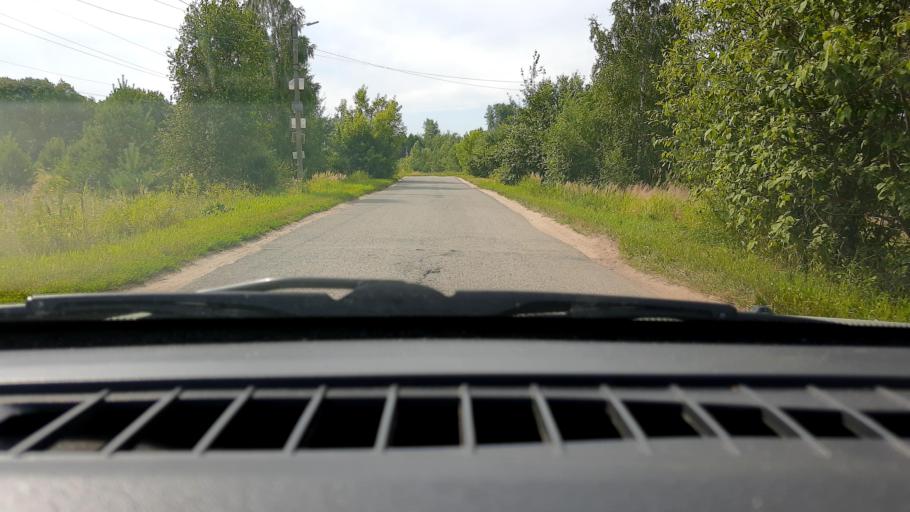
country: RU
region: Nizjnij Novgorod
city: Lukino
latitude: 56.4171
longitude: 43.7127
